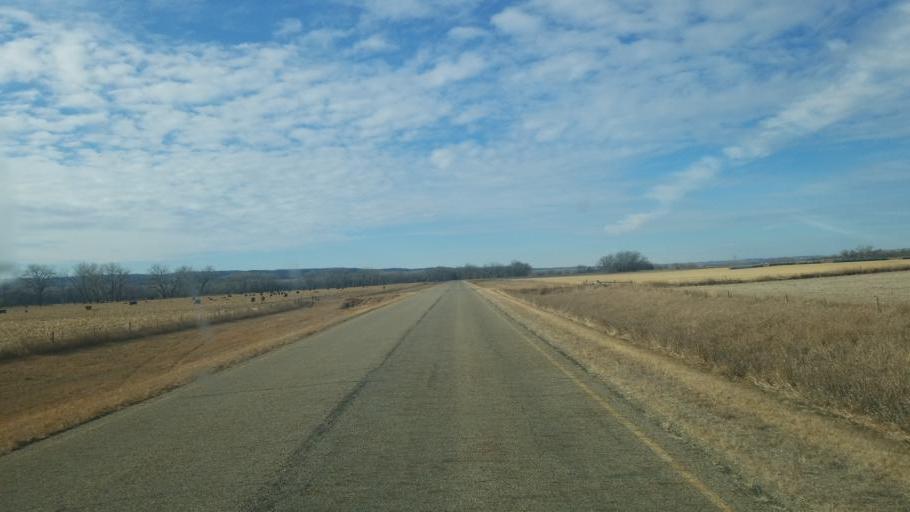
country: US
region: South Dakota
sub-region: Charles Mix County
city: Wagner
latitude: 42.8928
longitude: -98.2981
